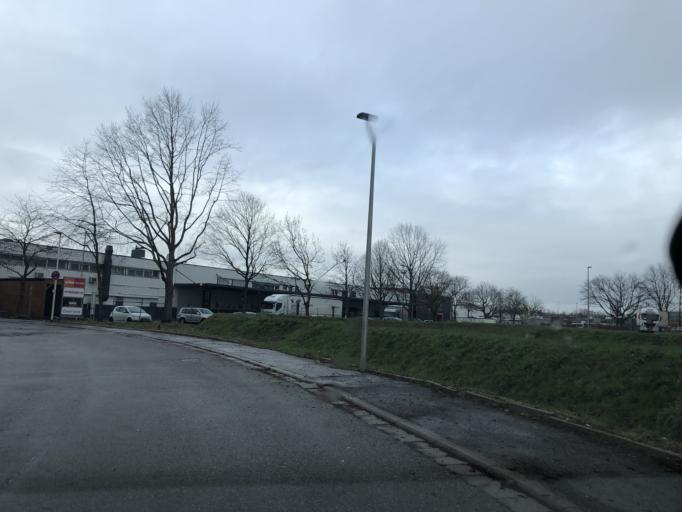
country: DE
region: Baden-Wuerttemberg
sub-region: Karlsruhe Region
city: Rastatt
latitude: 48.8581
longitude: 8.2358
